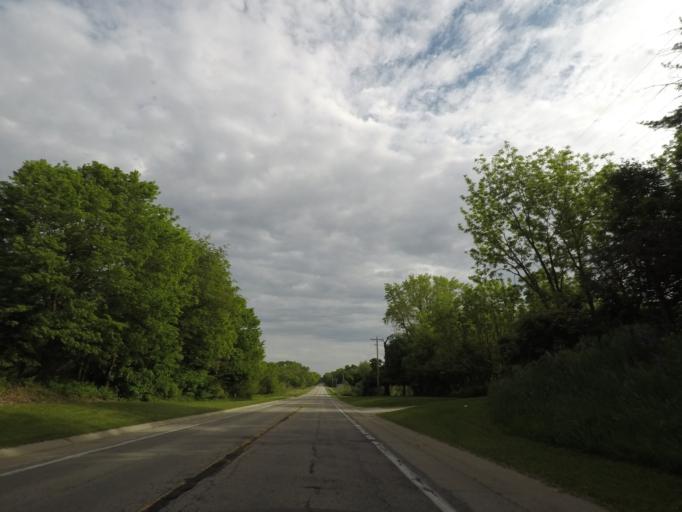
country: US
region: Illinois
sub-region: Logan County
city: Mount Pulaski
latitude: 40.0487
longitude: -89.2820
